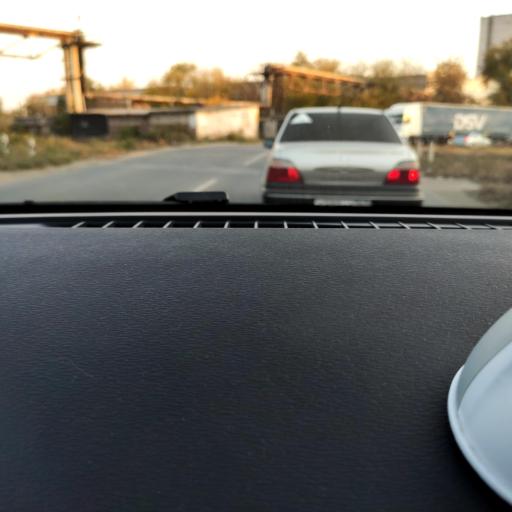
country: RU
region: Samara
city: Petra-Dubrava
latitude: 53.2387
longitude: 50.2882
